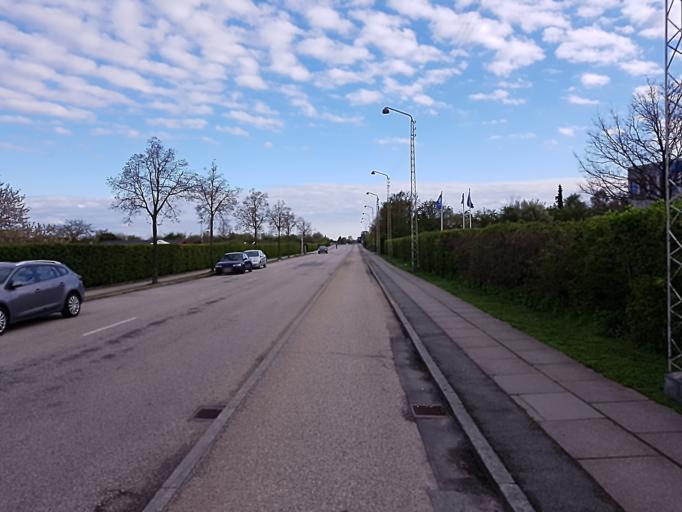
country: DK
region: Capital Region
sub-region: Tarnby Kommune
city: Tarnby
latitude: 55.6264
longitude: 12.5926
